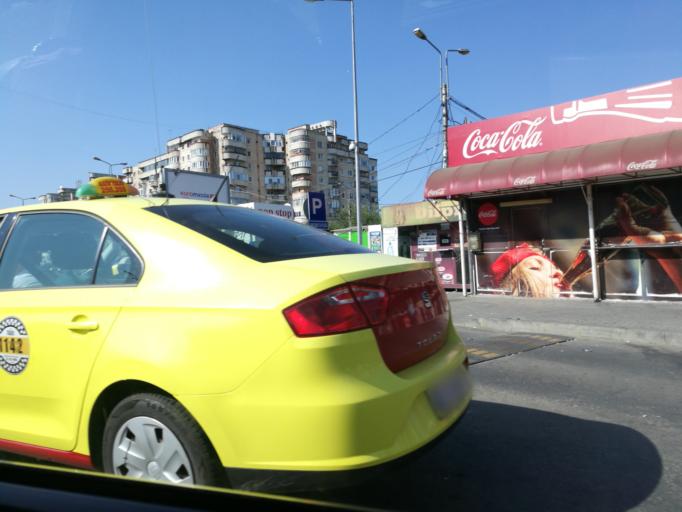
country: RO
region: Iasi
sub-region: Municipiul Iasi
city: Iasi
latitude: 47.1661
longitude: 27.5705
